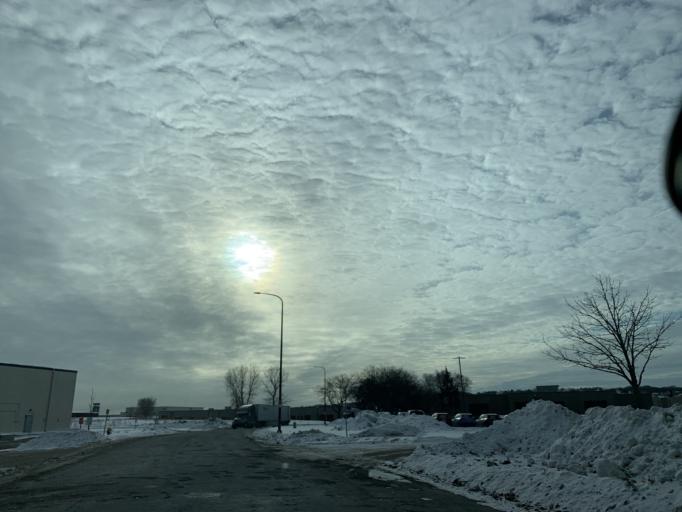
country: US
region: Minnesota
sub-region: Ramsey County
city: Saint Paul
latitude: 44.9397
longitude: -93.0725
